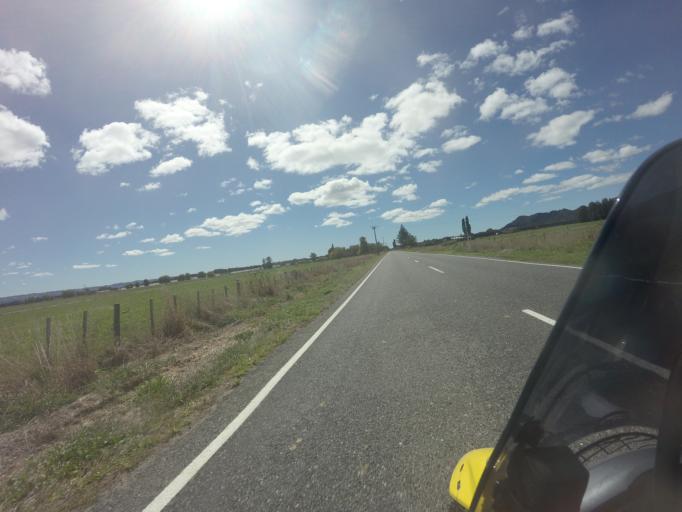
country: NZ
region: Bay of Plenty
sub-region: Whakatane District
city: Edgecumbe
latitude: -38.0449
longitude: 176.8304
